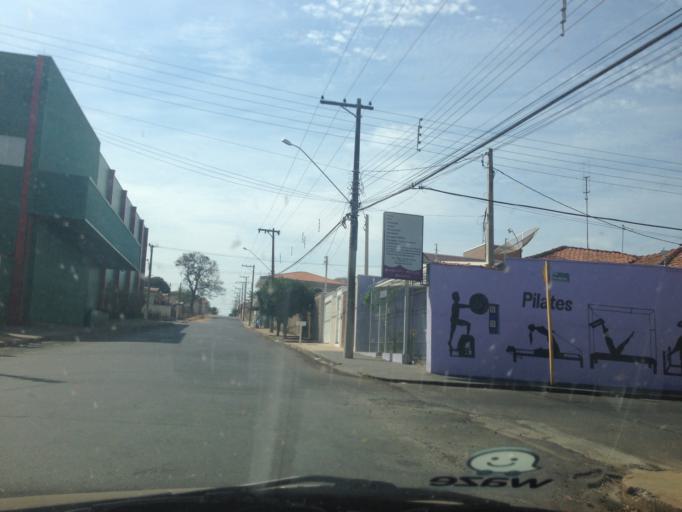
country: BR
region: Sao Paulo
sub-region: Casa Branca
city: Casa Branca
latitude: -21.7790
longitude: -47.0862
